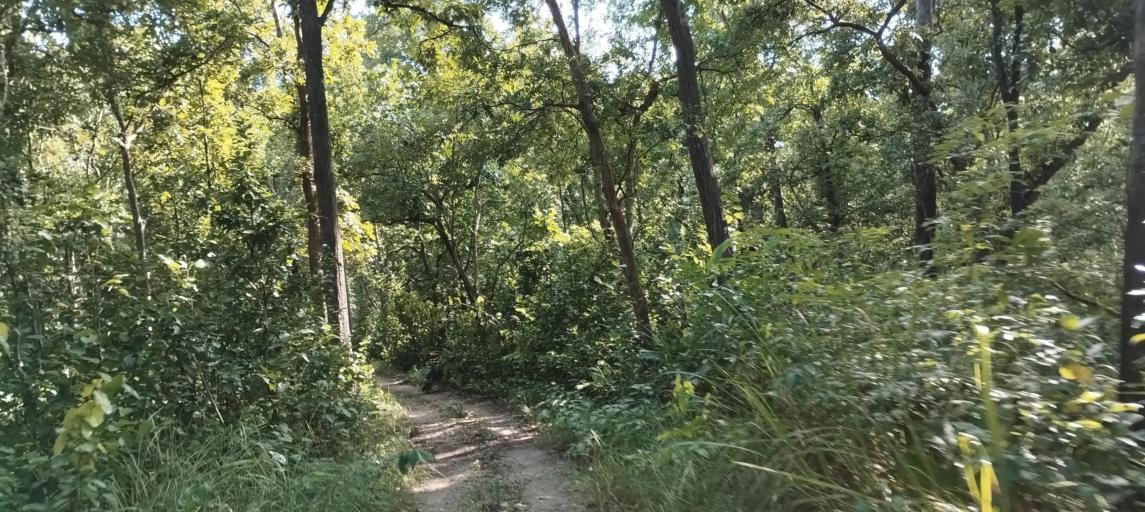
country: NP
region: Far Western
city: Tikapur
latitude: 28.5356
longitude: 81.2834
